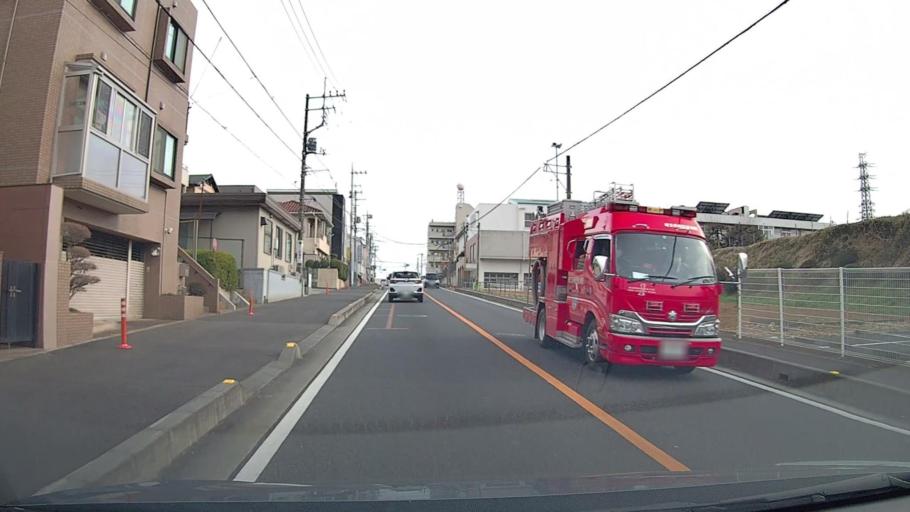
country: JP
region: Tokyo
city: Tanashicho
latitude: 35.7668
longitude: 139.5658
